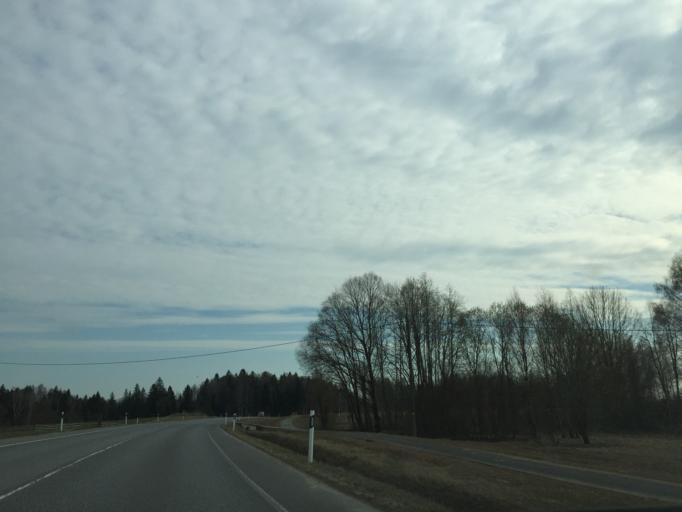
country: EE
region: Ida-Virumaa
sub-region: Johvi vald
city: Johvi
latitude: 59.2498
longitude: 27.5205
